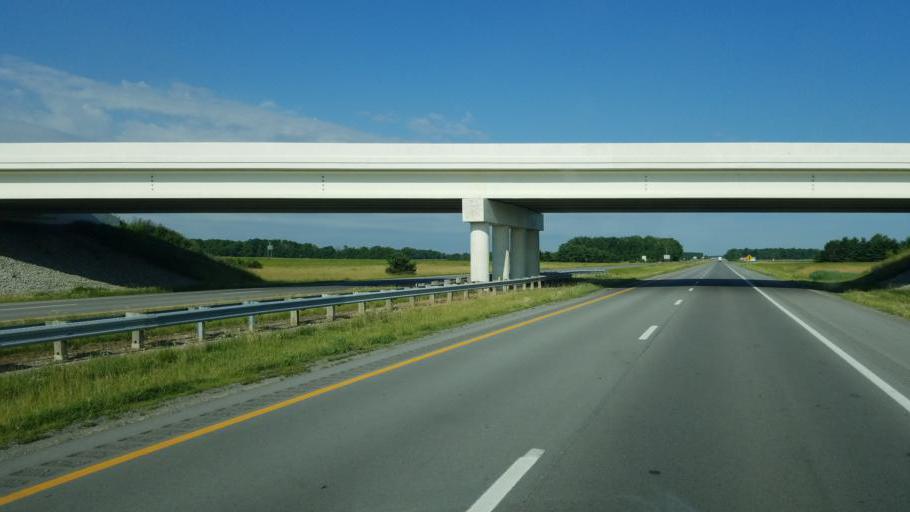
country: US
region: Ohio
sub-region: Hancock County
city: Findlay
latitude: 40.9858
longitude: -83.5748
